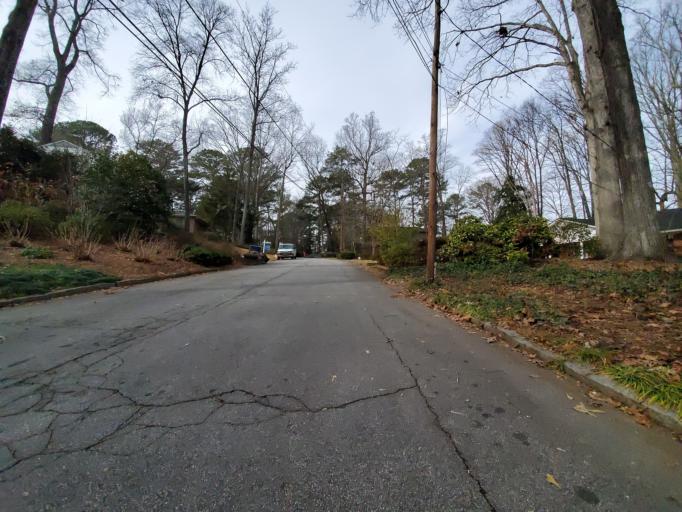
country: US
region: Georgia
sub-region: DeKalb County
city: North Decatur
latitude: 33.7818
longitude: -84.3139
